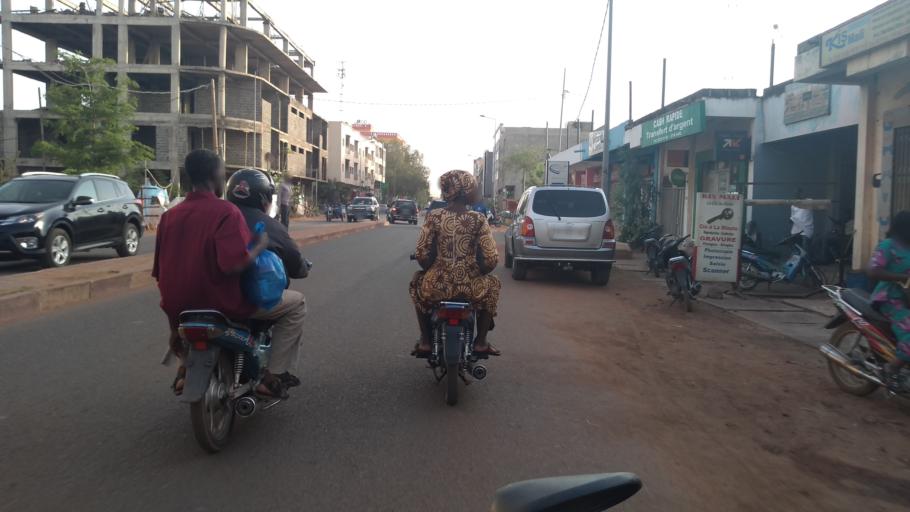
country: ML
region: Bamako
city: Bamako
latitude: 12.6291
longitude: -8.0318
